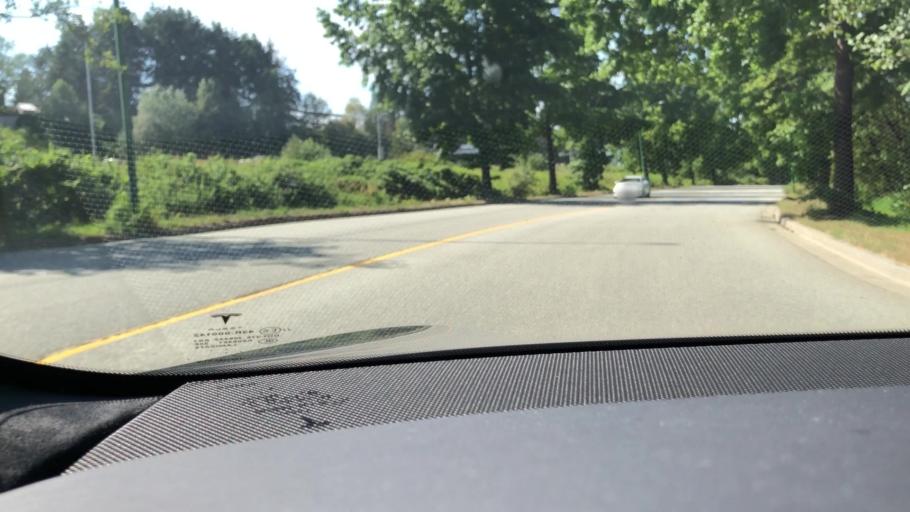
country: CA
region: British Columbia
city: Burnaby
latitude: 49.2516
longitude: -122.9739
